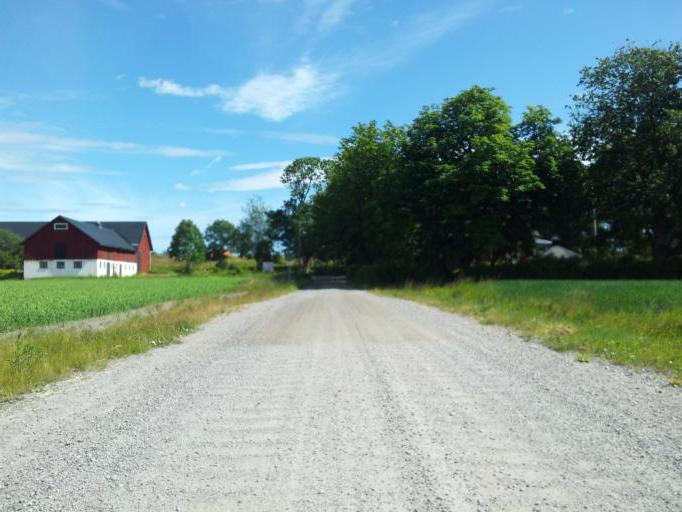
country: SE
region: Uppsala
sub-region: Uppsala Kommun
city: Saevja
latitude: 59.8635
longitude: 17.7227
